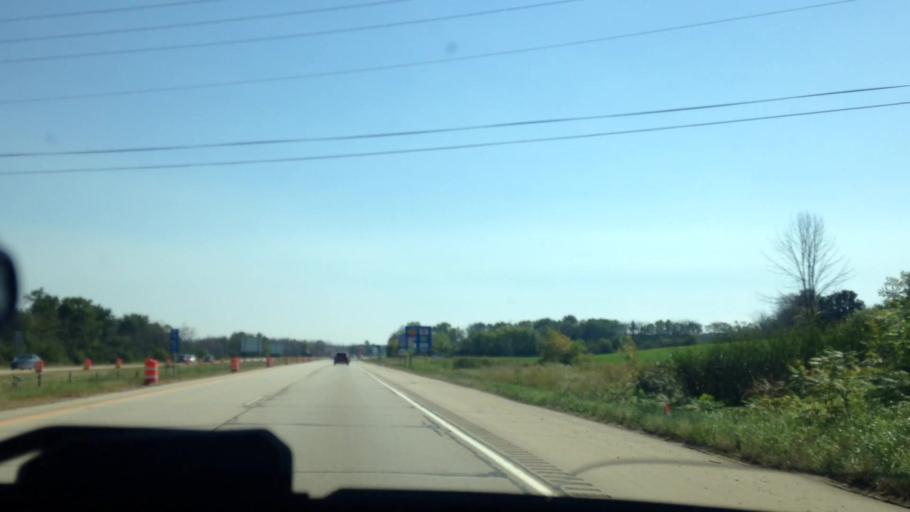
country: US
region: Wisconsin
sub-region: Ozaukee County
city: Grafton
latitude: 43.3313
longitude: -87.9224
